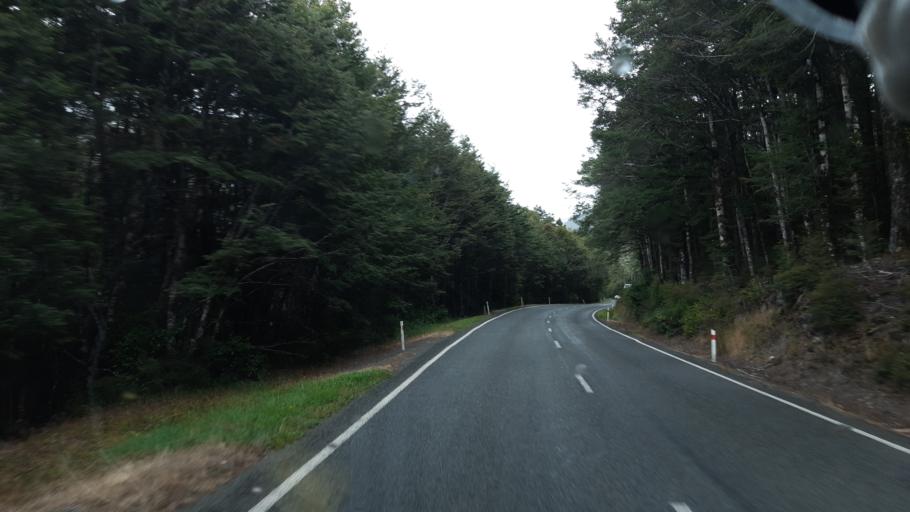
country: NZ
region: Canterbury
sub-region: Hurunui District
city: Amberley
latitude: -42.4506
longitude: 172.4035
